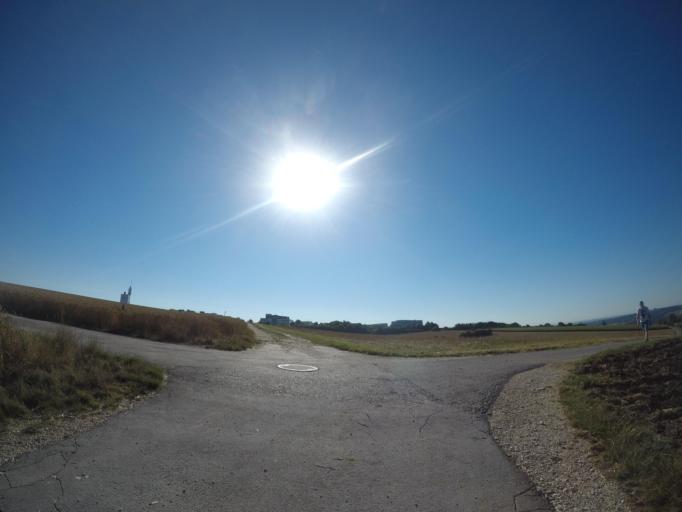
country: DE
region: Baden-Wuerttemberg
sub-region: Tuebingen Region
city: Dornstadt
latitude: 48.4214
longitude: 9.9280
